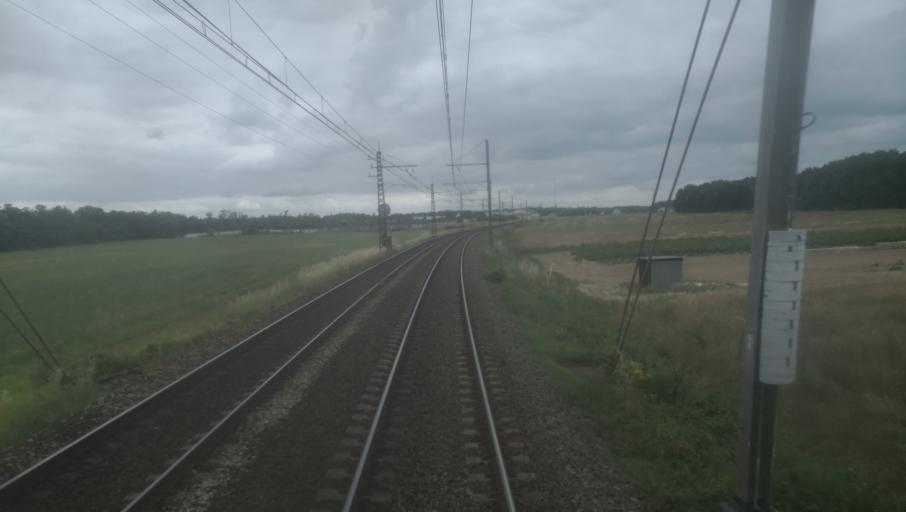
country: FR
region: Midi-Pyrenees
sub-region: Departement du Tarn-et-Garonne
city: Finhan
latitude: 43.9155
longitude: 1.2609
